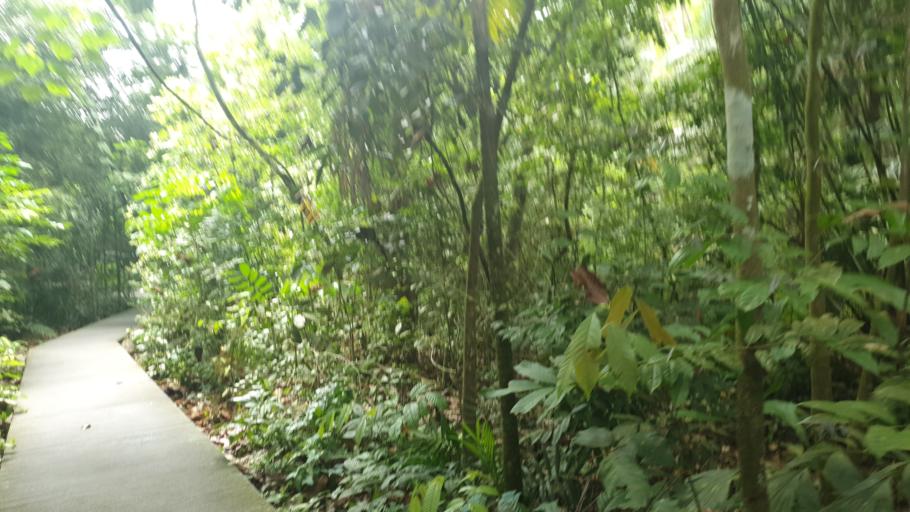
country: SG
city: Singapore
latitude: 1.3606
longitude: 103.8249
